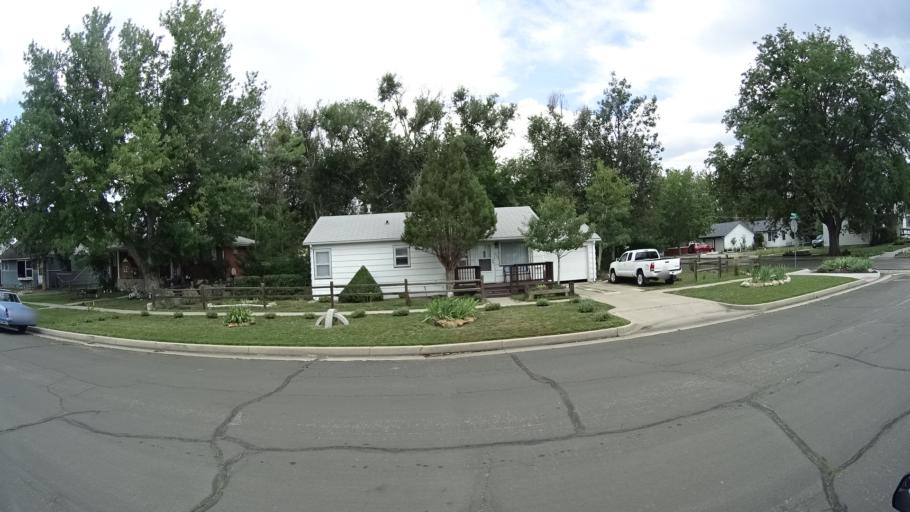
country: US
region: Colorado
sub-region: El Paso County
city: Colorado Springs
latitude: 38.8644
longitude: -104.8132
